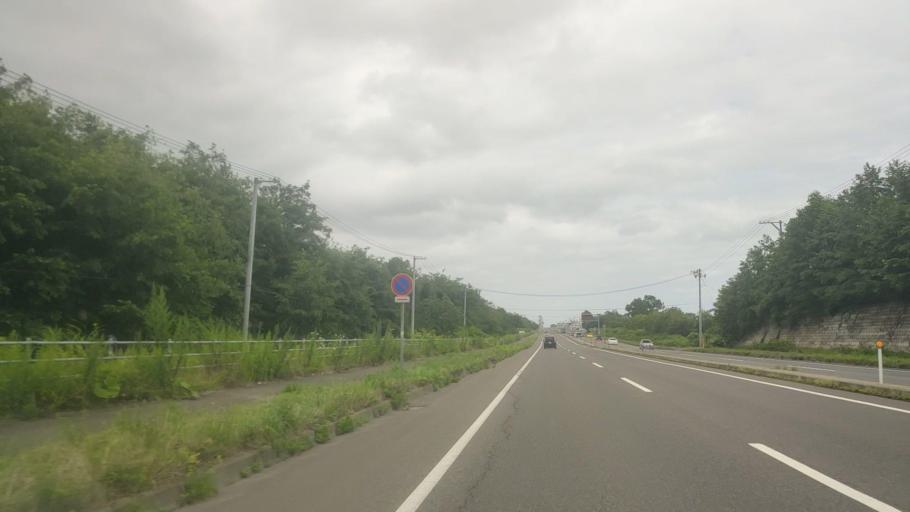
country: JP
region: Hokkaido
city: Shiraoi
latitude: 42.4592
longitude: 141.2015
